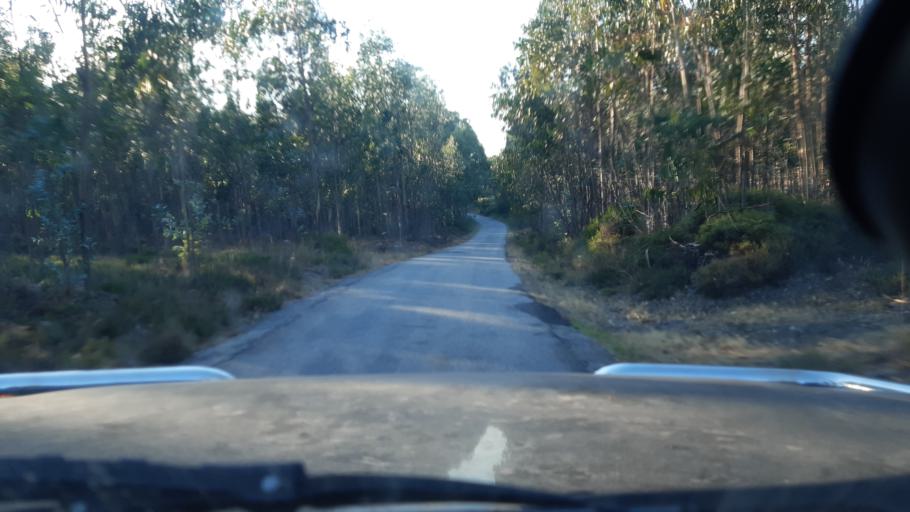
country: PT
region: Viseu
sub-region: Mortagua
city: Mortagua
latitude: 40.5429
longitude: -8.2547
